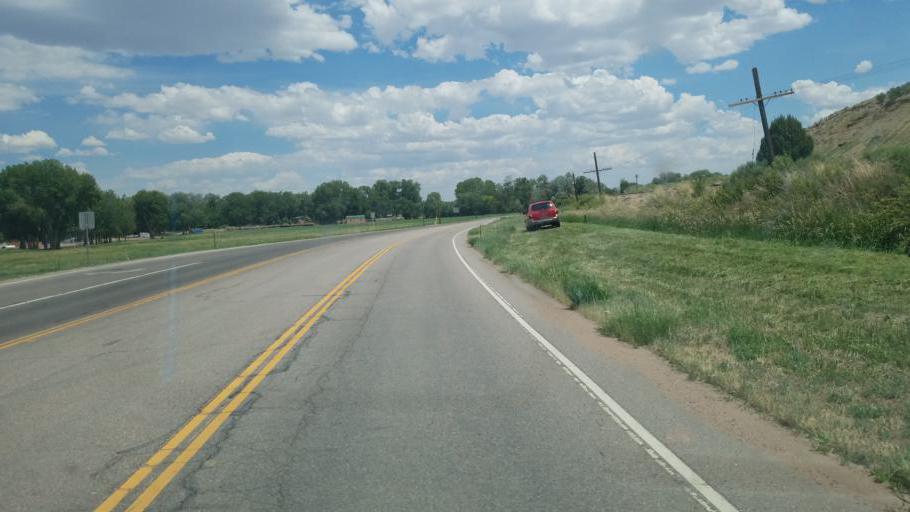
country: US
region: Colorado
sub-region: Fremont County
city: Florence
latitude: 38.4053
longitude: -105.1452
